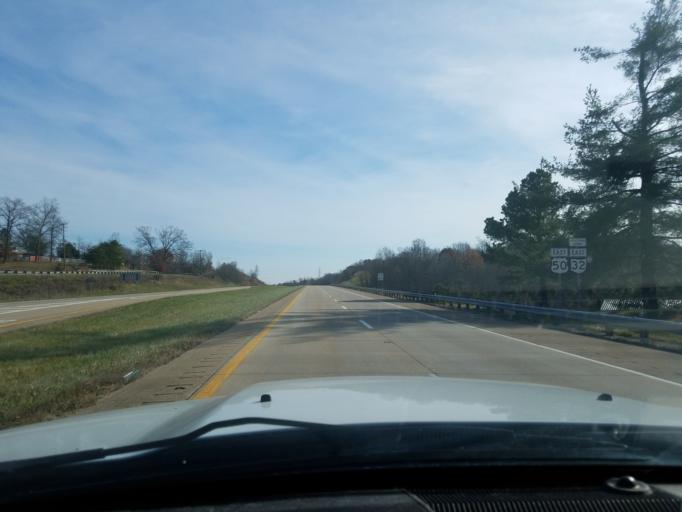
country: US
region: West Virginia
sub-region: Wood County
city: Washington
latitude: 39.2213
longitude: -81.8674
